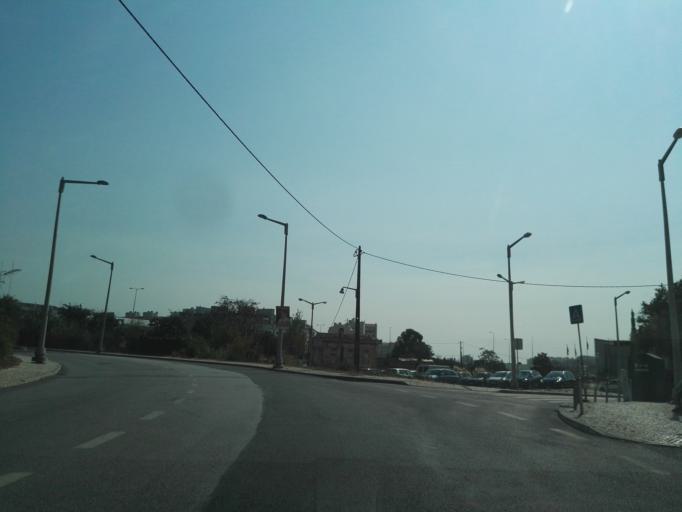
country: PT
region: Lisbon
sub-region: Loures
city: Moscavide
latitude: 38.7524
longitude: -9.1053
